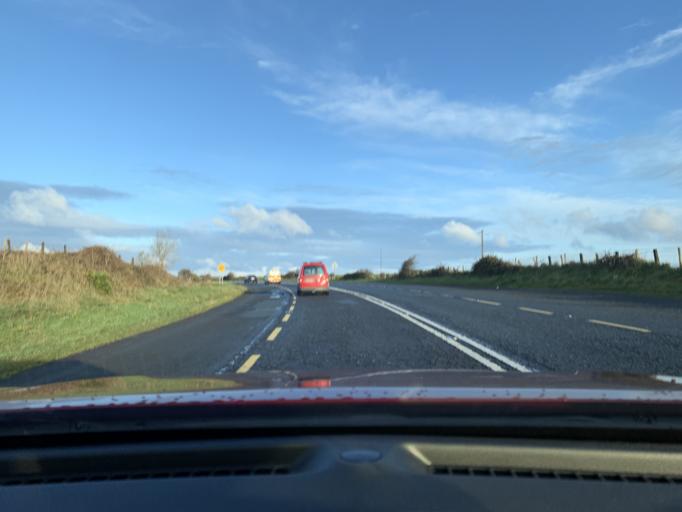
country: IE
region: Connaught
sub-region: Sligo
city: Sligo
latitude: 54.3647
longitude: -8.5273
